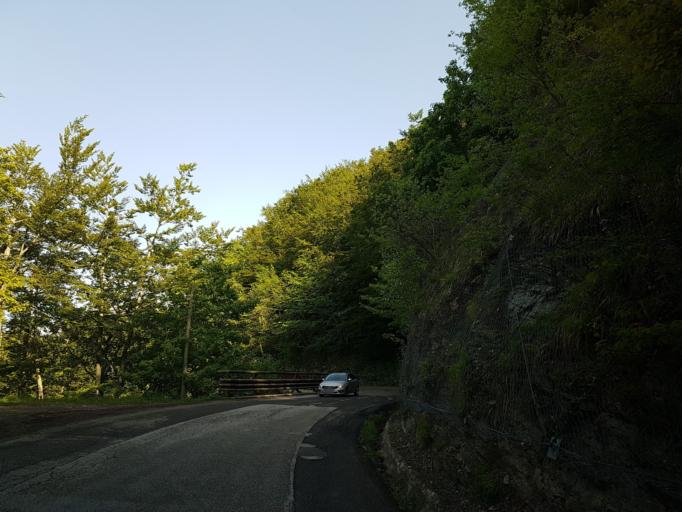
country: IT
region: Emilia-Romagna
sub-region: Forli-Cesena
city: San Piero in Bagno
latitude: 43.8101
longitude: 11.9187
